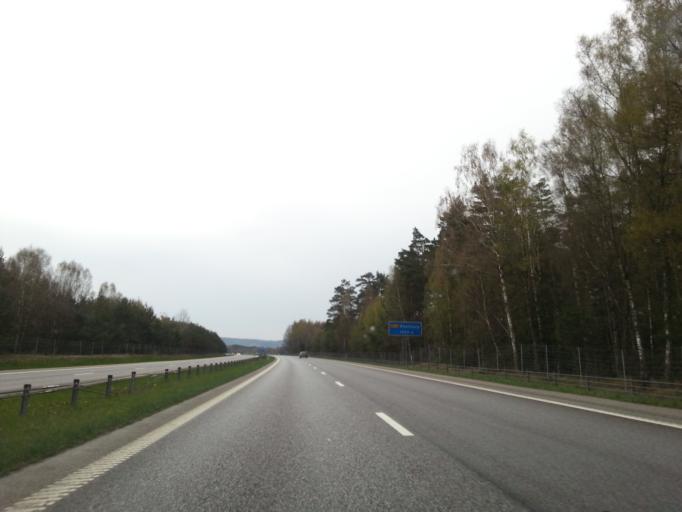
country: SE
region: Halland
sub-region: Laholms Kommun
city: Mellbystrand
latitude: 56.4675
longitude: 12.9413
